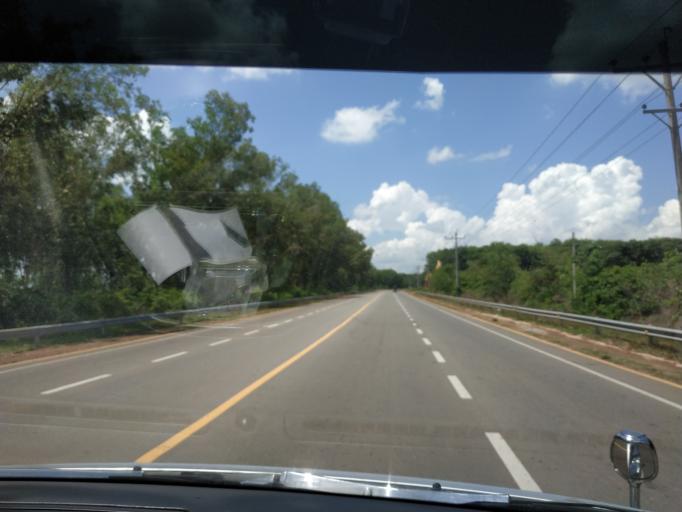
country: MM
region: Mon
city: Kyaikto
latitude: 17.3199
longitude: 97.0206
